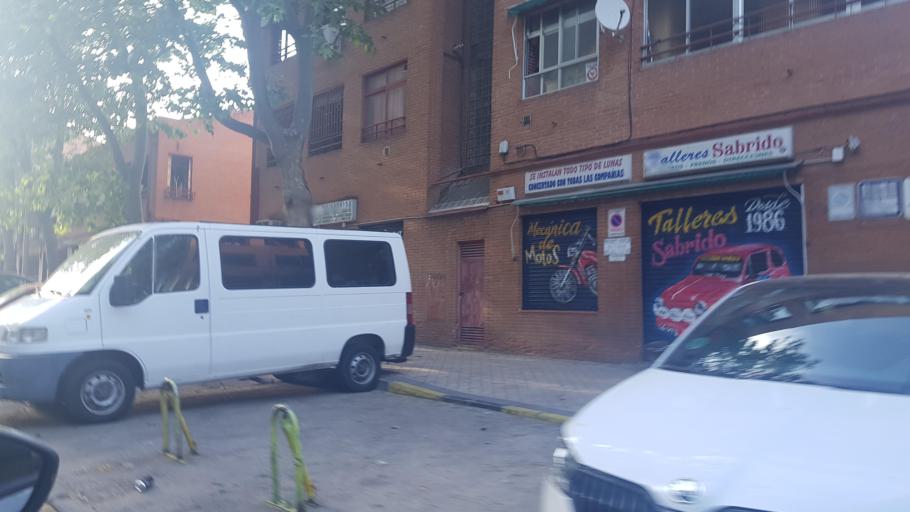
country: ES
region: Madrid
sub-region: Provincia de Madrid
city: Puente de Vallecas
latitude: 40.3710
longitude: -3.6603
